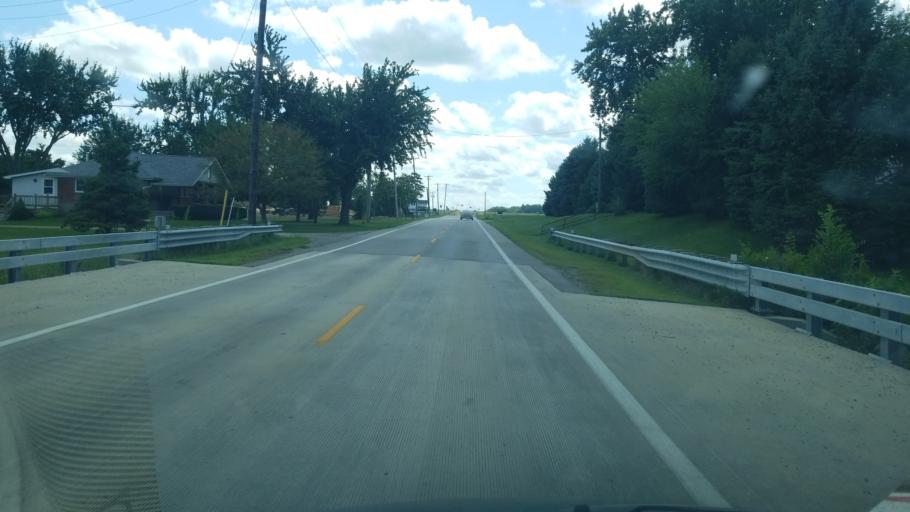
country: US
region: Ohio
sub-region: Henry County
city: Liberty Center
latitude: 41.4386
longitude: -84.0089
